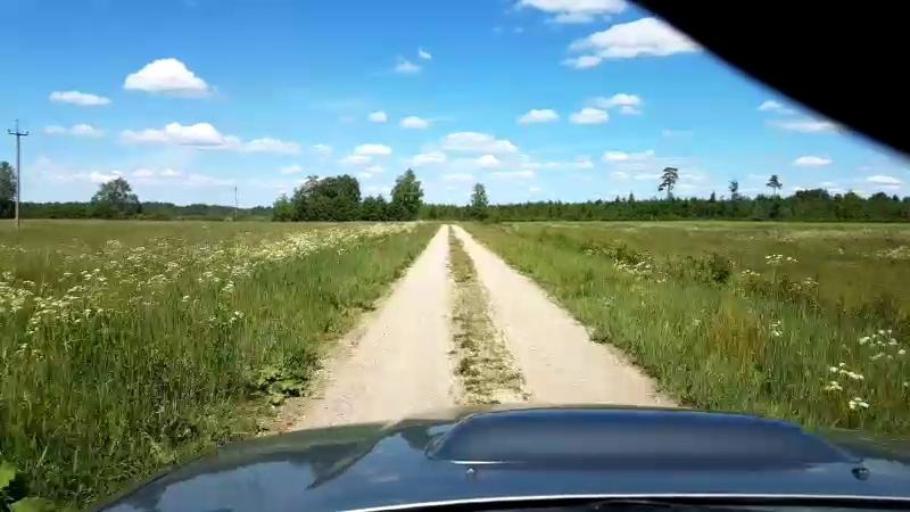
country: EE
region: Paernumaa
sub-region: Halinga vald
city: Parnu-Jaagupi
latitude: 58.5355
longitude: 24.5300
